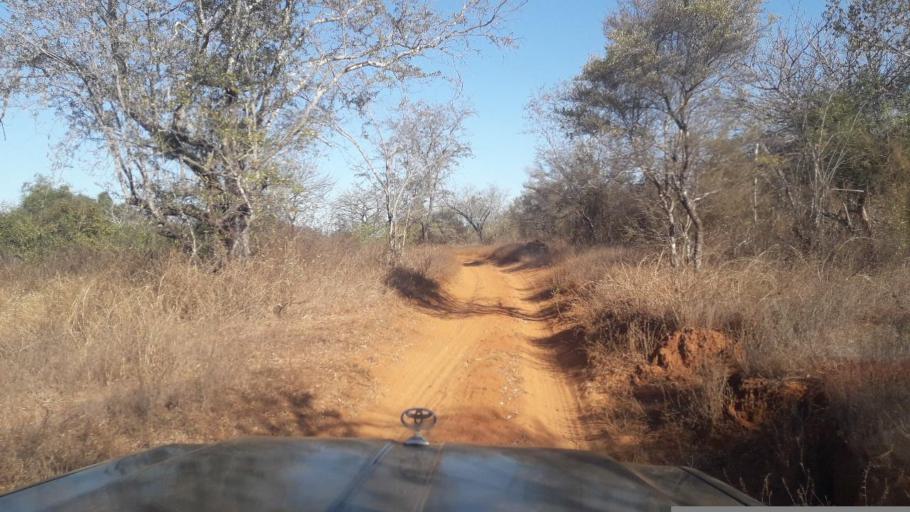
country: MG
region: Boeny
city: Sitampiky
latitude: -16.4242
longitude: 45.6206
